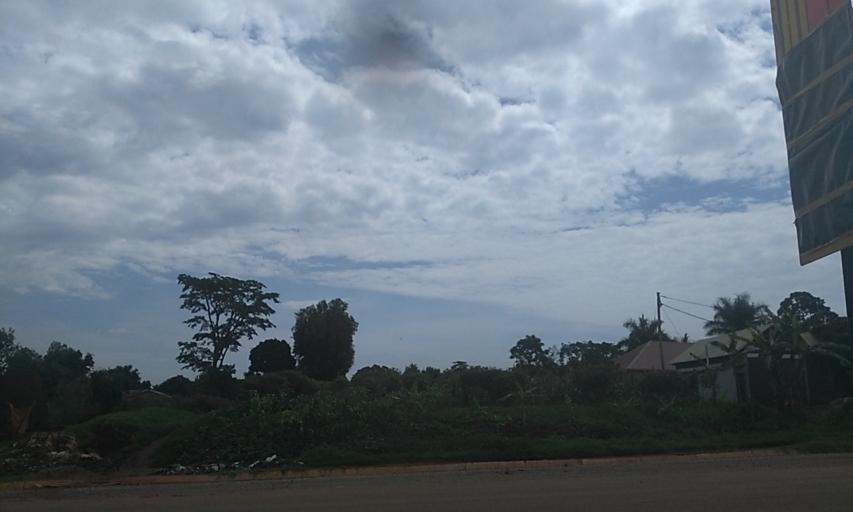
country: UG
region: Central Region
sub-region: Wakiso District
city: Kireka
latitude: 0.3658
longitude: 32.6430
